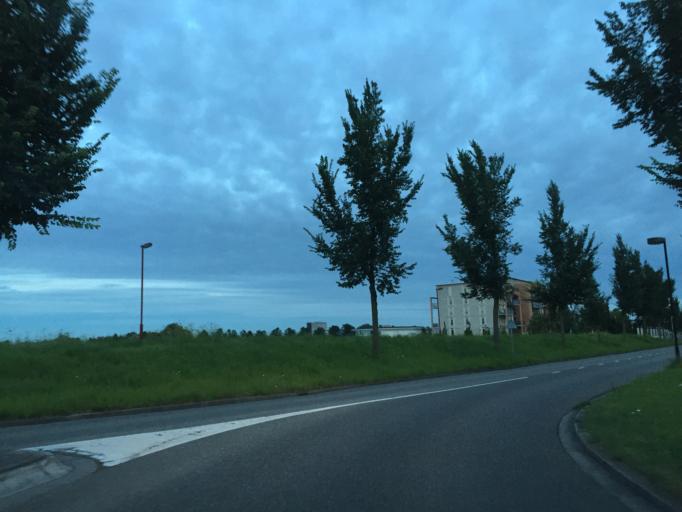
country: NL
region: South Holland
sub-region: Gemeente Rijnwoude
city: Benthuizen
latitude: 52.0774
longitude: 4.5291
